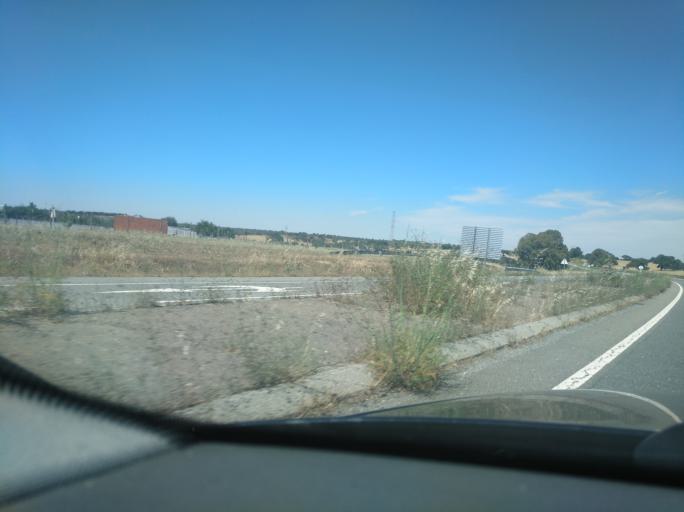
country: PT
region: Beja
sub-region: Ourique
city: Ourique
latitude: 37.6623
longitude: -8.1750
